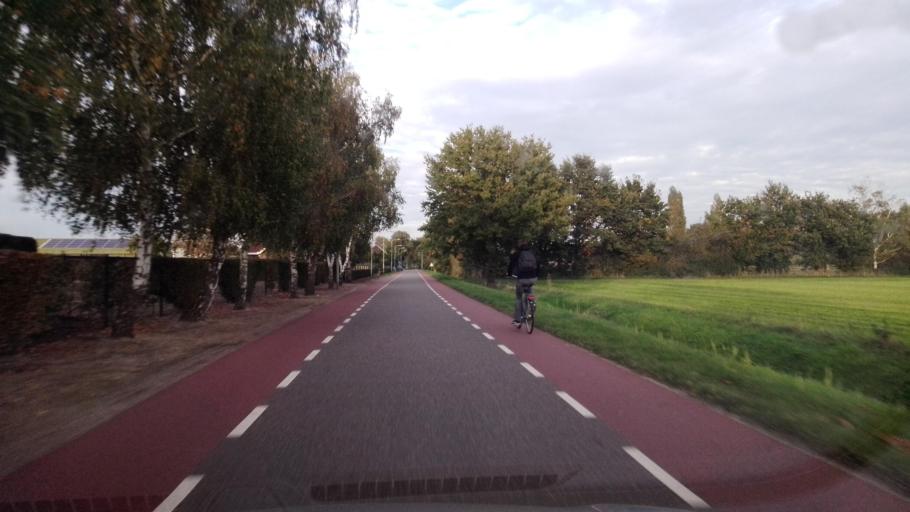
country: NL
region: Limburg
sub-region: Gemeente Venlo
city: Tegelen
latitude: 51.3229
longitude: 6.1331
